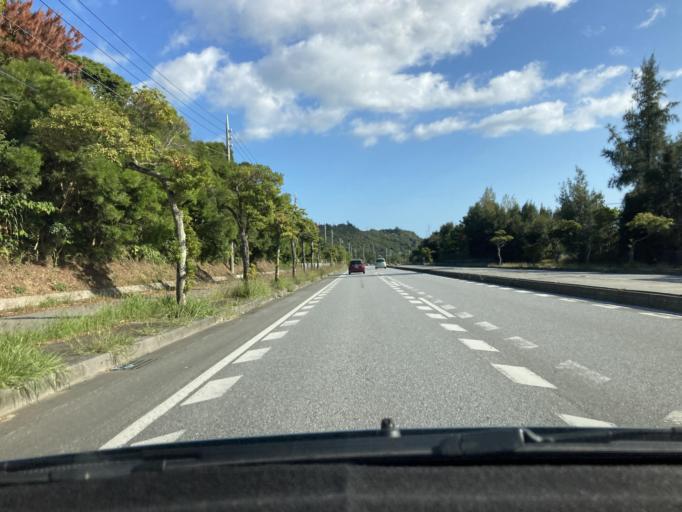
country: JP
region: Okinawa
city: Ishikawa
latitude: 26.4027
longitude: 127.8259
